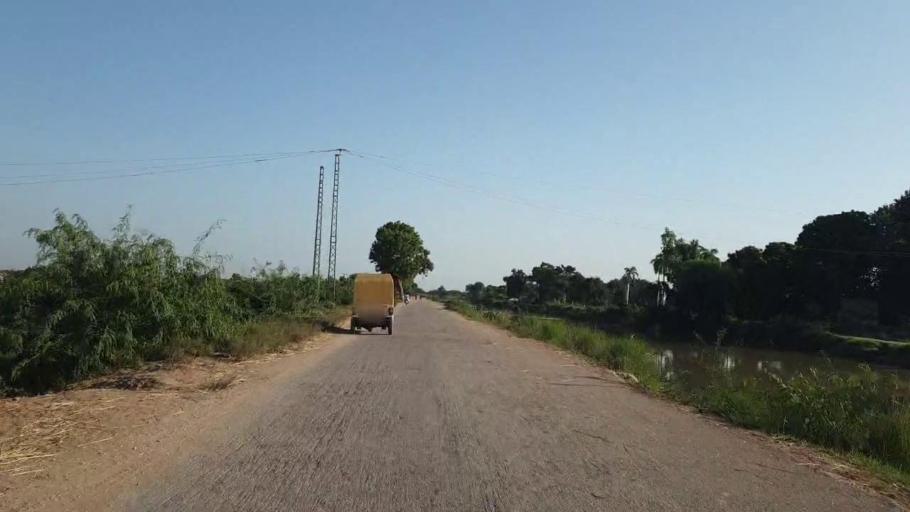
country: PK
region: Sindh
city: Hyderabad
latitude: 25.3090
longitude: 68.4327
